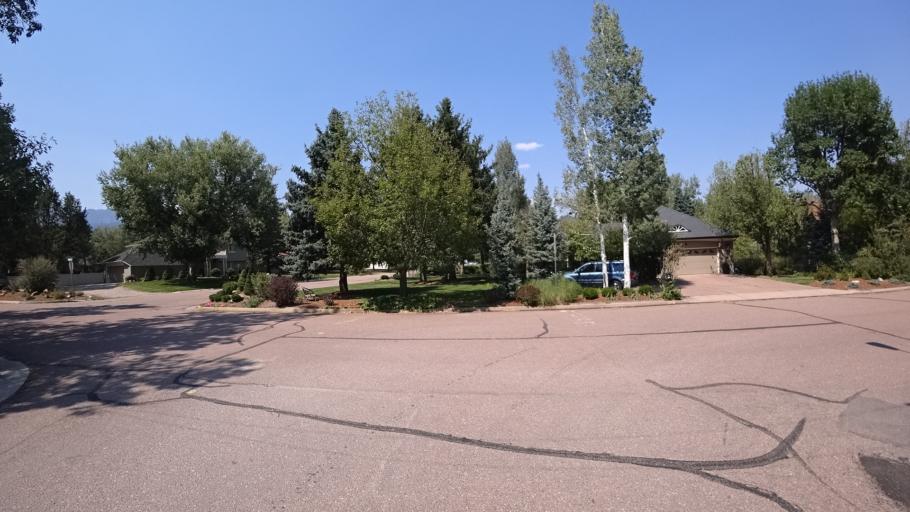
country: US
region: Colorado
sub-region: El Paso County
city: Colorado Springs
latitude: 38.7916
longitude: -104.8398
